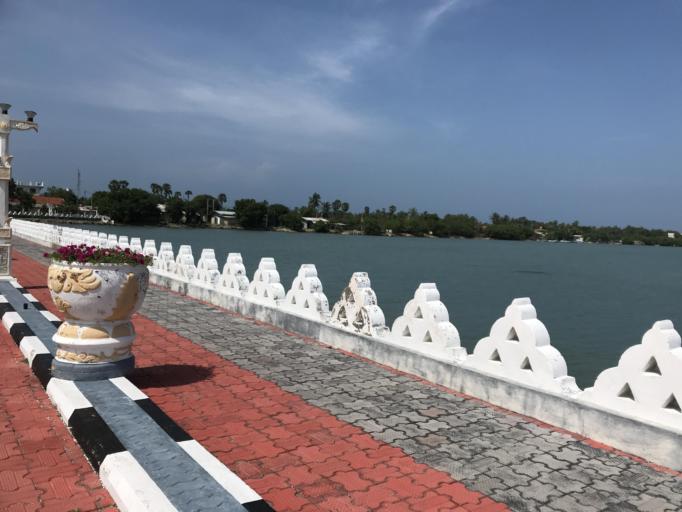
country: LK
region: Northern Province
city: Jaffna
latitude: 9.6126
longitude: 79.7760
